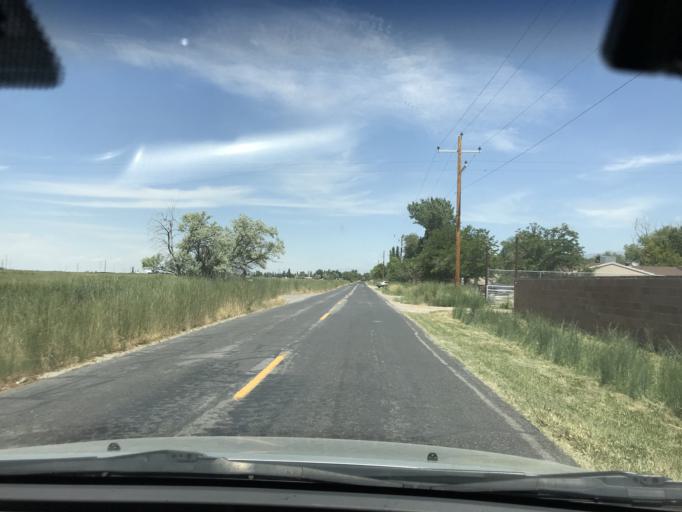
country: US
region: Utah
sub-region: Davis County
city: North Salt Lake
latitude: 40.8272
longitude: -111.9535
